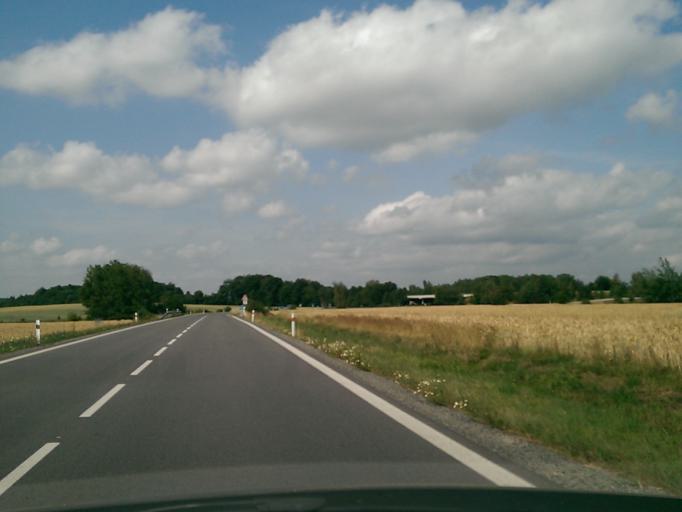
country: CZ
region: Central Bohemia
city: Bakov nad Jizerou
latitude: 50.4820
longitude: 14.9702
